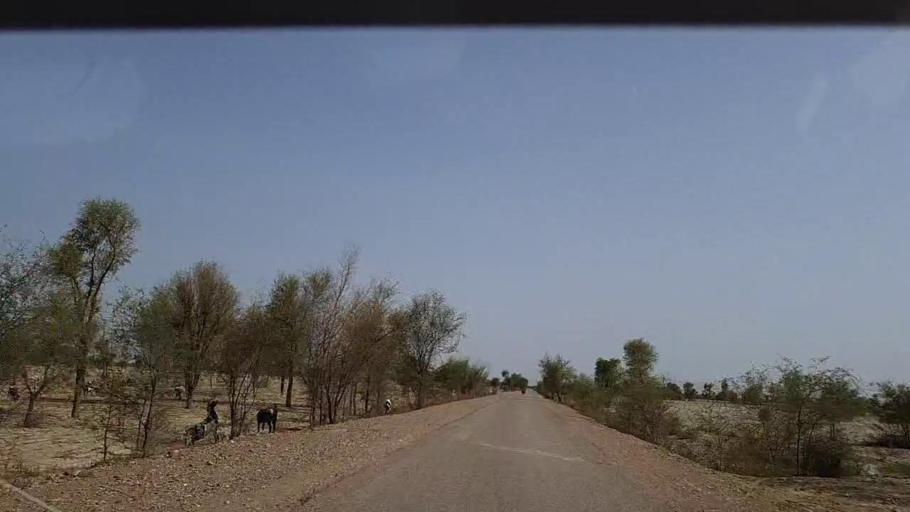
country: PK
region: Sindh
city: Johi
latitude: 26.6286
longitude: 67.5009
